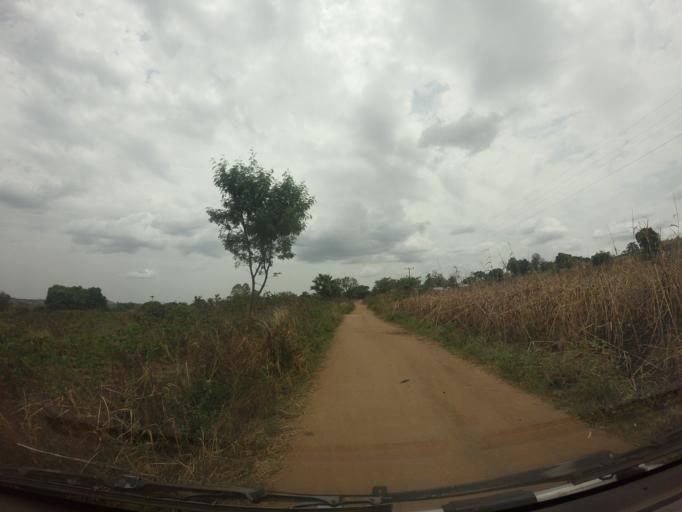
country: UG
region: Northern Region
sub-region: Arua District
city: Arua
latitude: 2.9470
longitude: 30.9395
